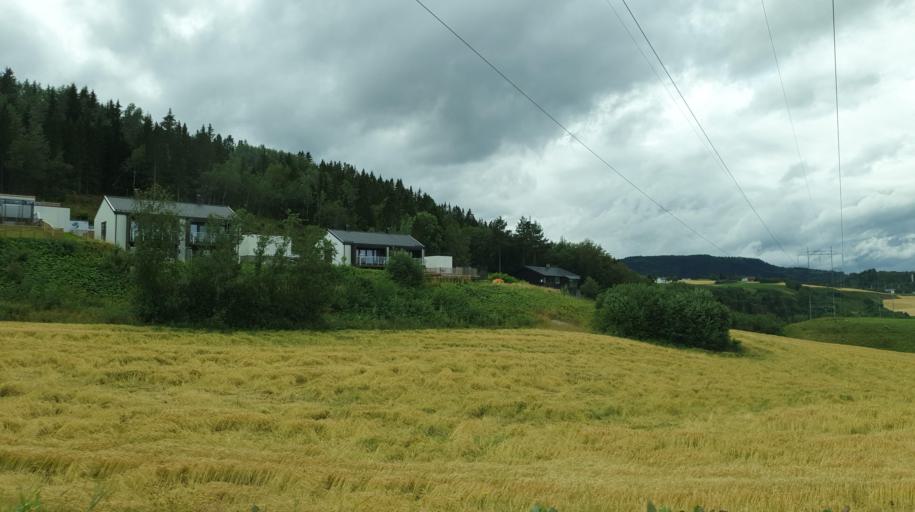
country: NO
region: Nord-Trondelag
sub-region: Stjordal
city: Stjordalshalsen
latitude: 63.4330
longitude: 10.9536
